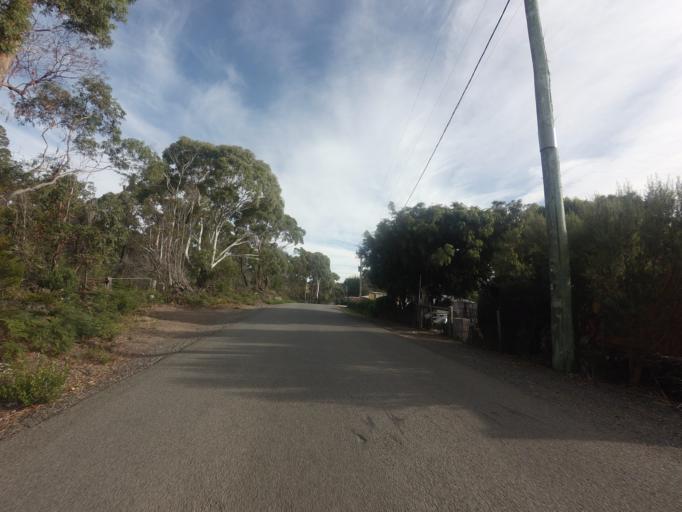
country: AU
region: Tasmania
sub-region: Sorell
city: Sorell
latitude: -42.9618
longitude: 147.8373
